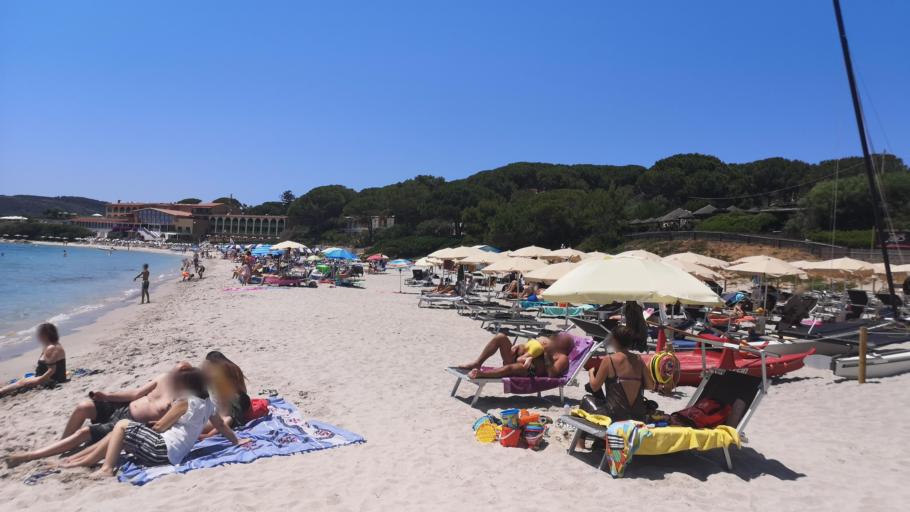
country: IT
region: Sardinia
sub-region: Provincia di Sassari
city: Alghero
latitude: 40.5842
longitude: 8.2584
